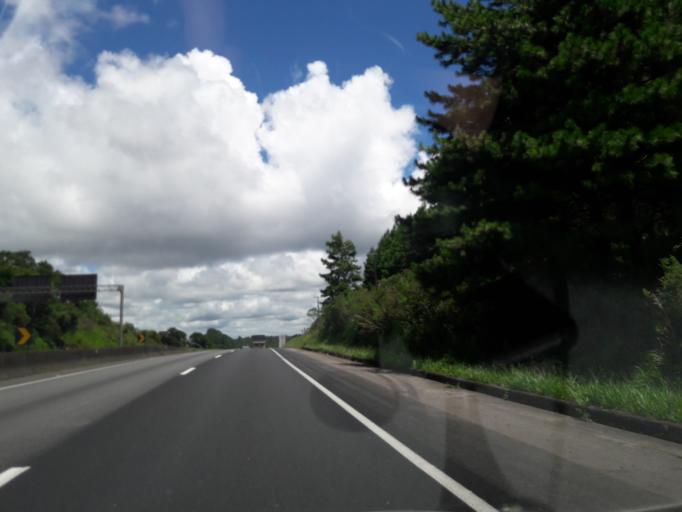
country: BR
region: Parana
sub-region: Campina Grande Do Sul
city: Campina Grande do Sul
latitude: -25.1754
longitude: -48.8708
